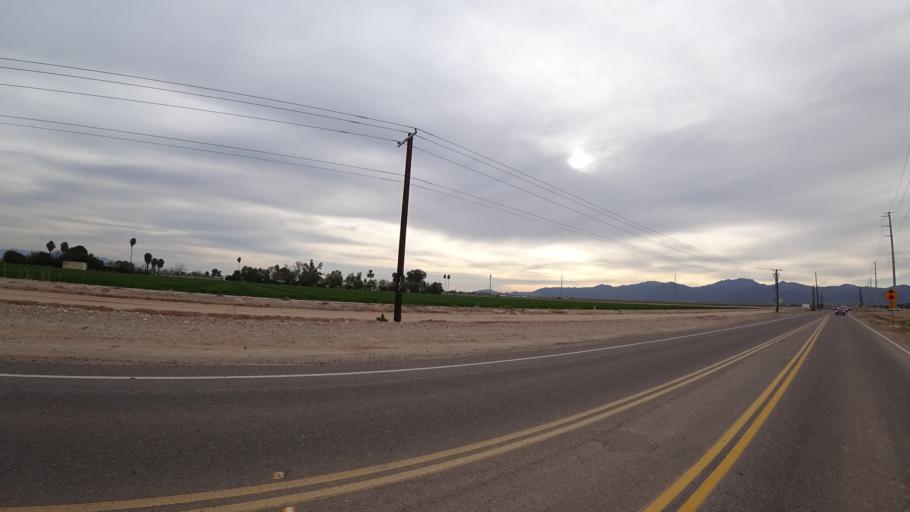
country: US
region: Arizona
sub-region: Maricopa County
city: Citrus Park
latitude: 33.5953
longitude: -112.4245
